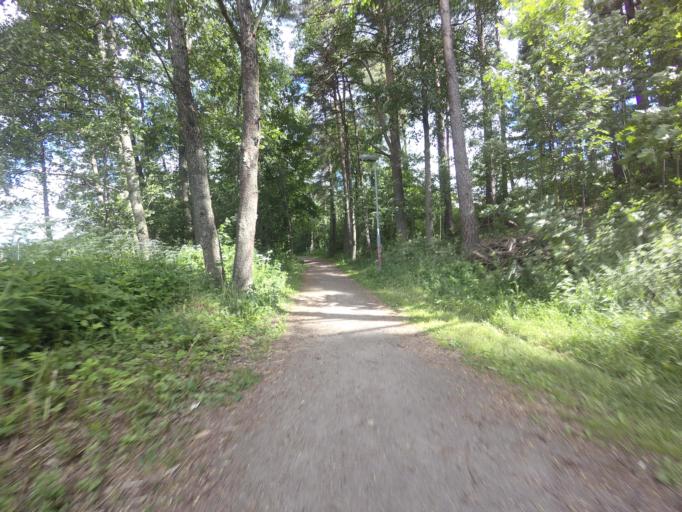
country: FI
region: Uusimaa
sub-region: Helsinki
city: Espoo
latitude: 60.1542
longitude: 24.6263
